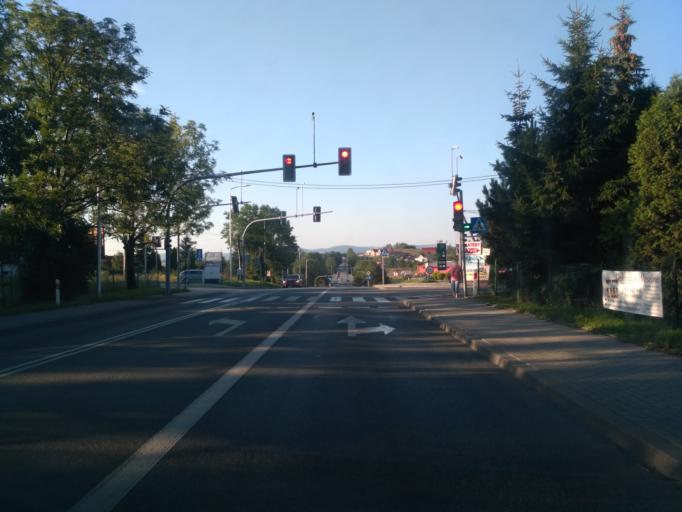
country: PL
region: Subcarpathian Voivodeship
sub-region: Krosno
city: Krosno
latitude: 49.6675
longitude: 21.7769
